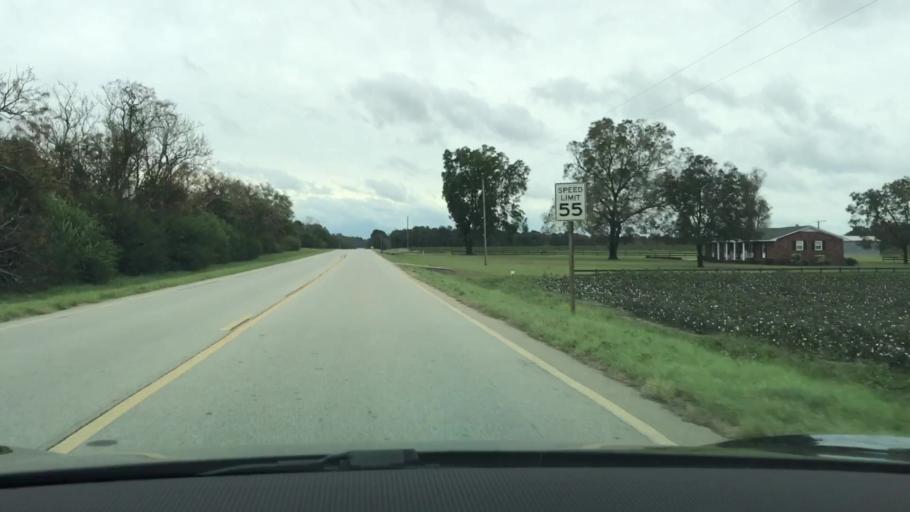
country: US
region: Georgia
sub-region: Jefferson County
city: Wrens
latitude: 33.2003
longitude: -82.4655
